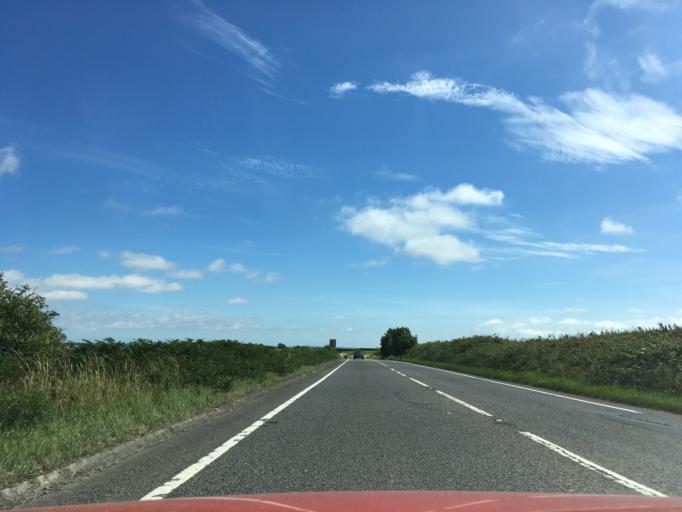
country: GB
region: England
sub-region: Dorset
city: Dorchester
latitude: 50.7955
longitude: -2.5485
